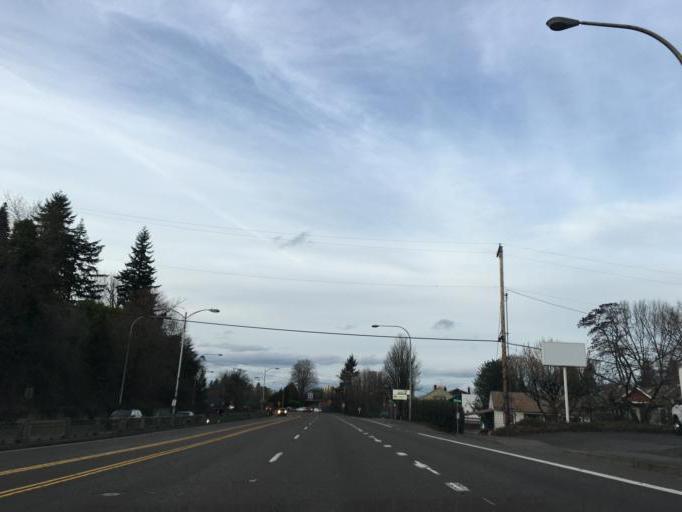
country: US
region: Oregon
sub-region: Multnomah County
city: Portland
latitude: 45.4934
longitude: -122.6769
